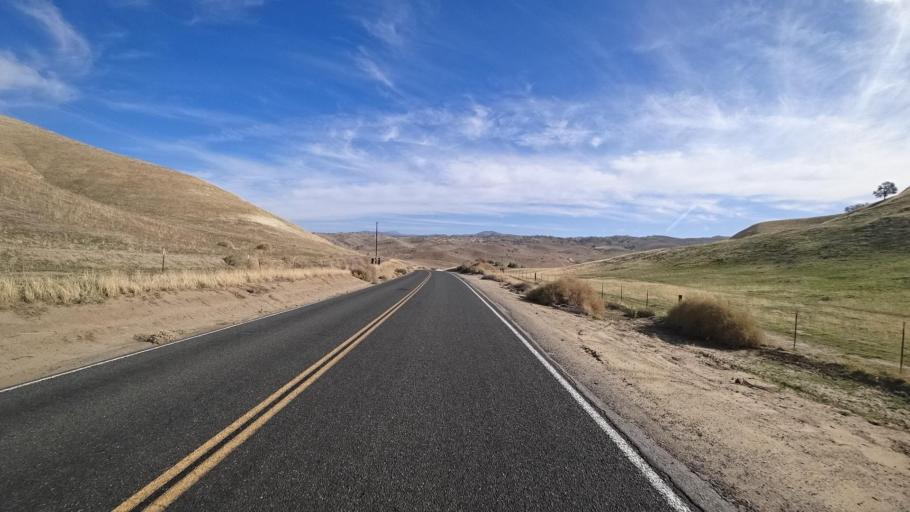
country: US
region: California
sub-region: Kern County
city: Oildale
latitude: 35.6112
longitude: -118.8858
